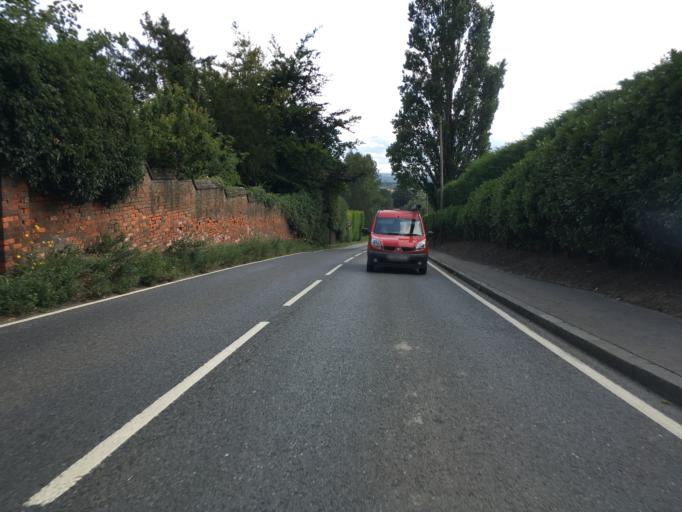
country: GB
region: England
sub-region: Kent
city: Headcorn
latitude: 51.2117
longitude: 0.5903
